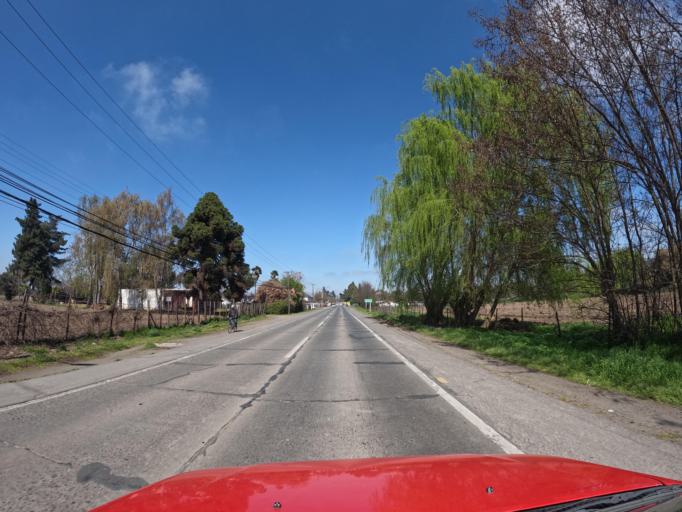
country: CL
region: Maule
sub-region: Provincia de Curico
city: Molina
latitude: -35.0705
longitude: -71.2558
